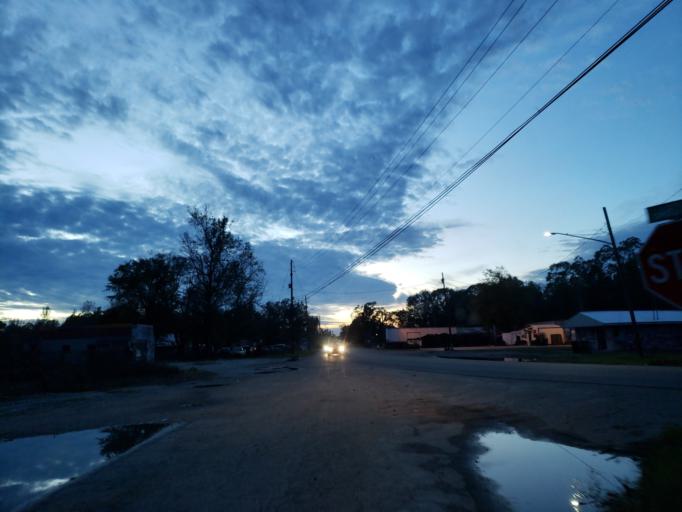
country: US
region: Mississippi
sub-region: Forrest County
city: Hattiesburg
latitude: 31.3251
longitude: -89.2704
